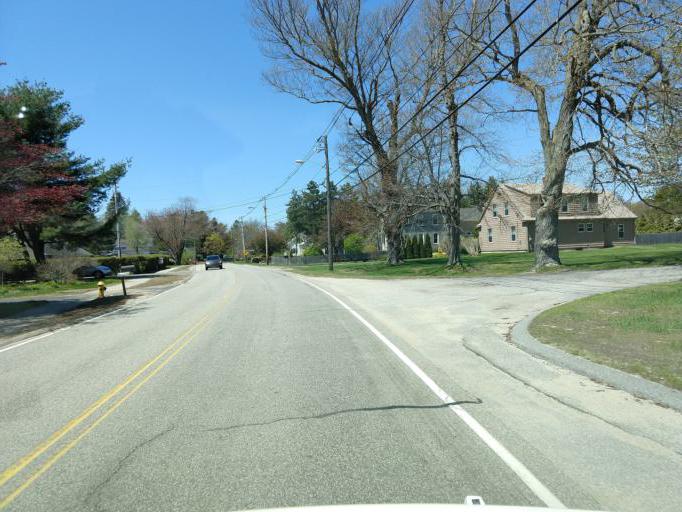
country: US
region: Maine
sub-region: York County
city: Saco
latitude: 43.4819
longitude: -70.4067
